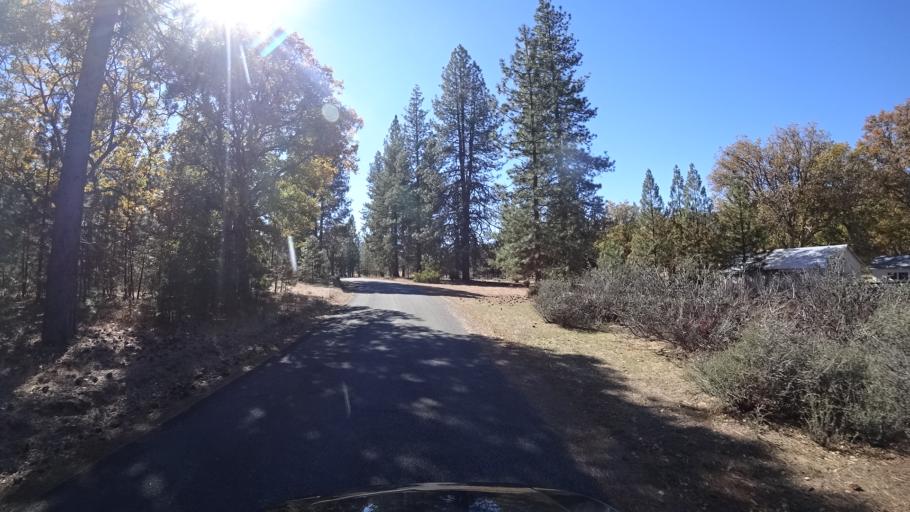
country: US
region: California
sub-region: Siskiyou County
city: Yreka
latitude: 41.5881
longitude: -122.9041
